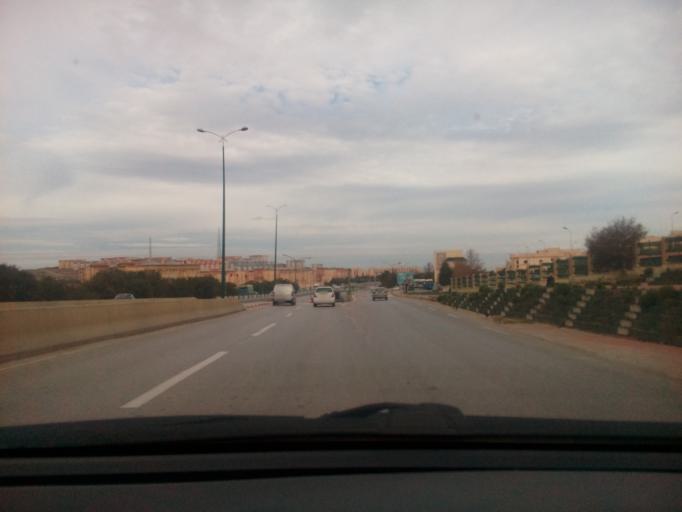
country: DZ
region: Tlemcen
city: Mansoura
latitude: 34.8917
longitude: -1.3555
